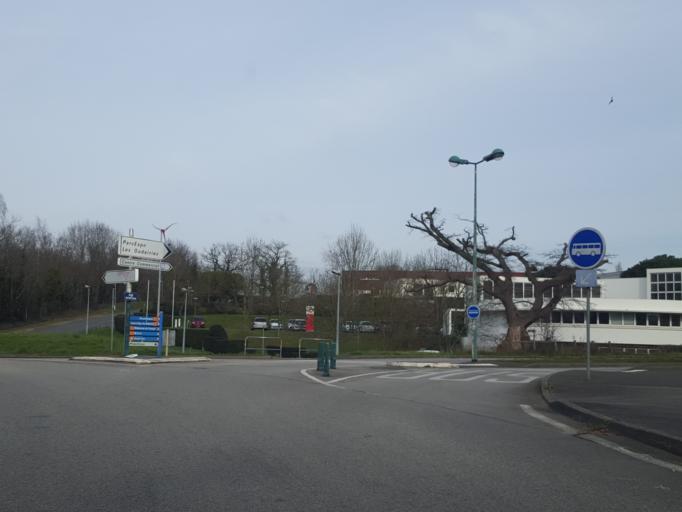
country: FR
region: Pays de la Loire
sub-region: Departement de la Vendee
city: La Roche-sur-Yon
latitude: 46.6693
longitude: -1.4094
